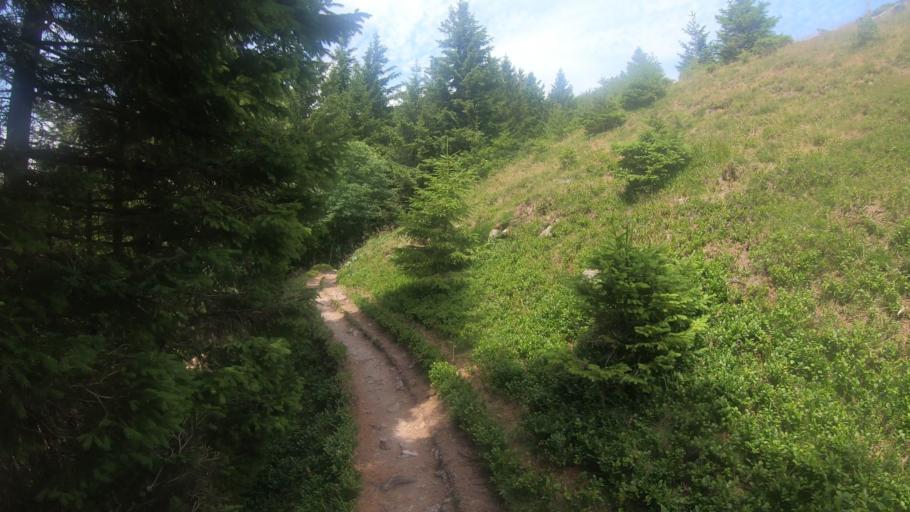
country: FR
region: Alsace
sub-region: Departement du Haut-Rhin
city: Metzeral
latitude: 48.0498
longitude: 7.0227
